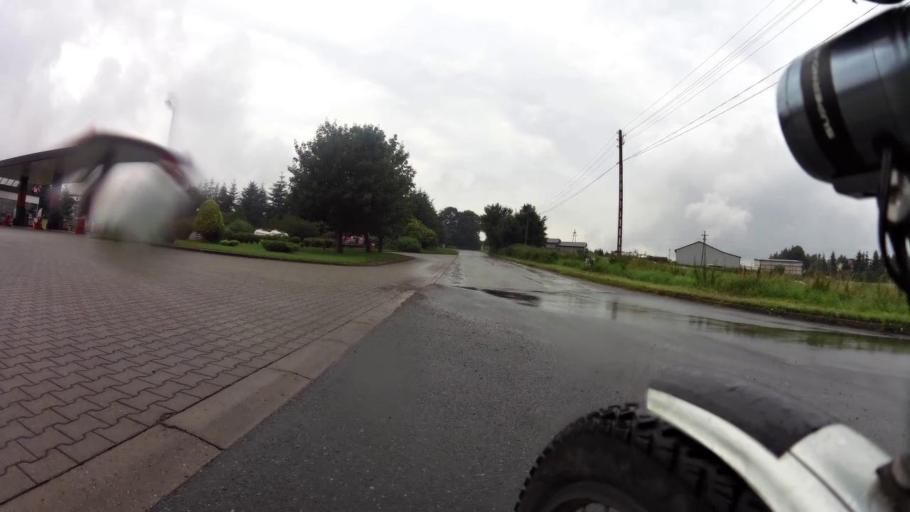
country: PL
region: West Pomeranian Voivodeship
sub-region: Powiat gryfinski
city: Banie
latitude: 53.1019
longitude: 14.6517
